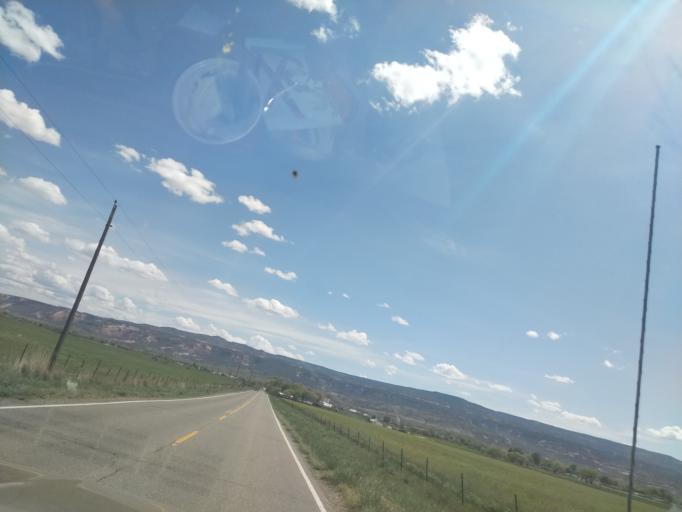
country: US
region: Colorado
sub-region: Mesa County
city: Fruita
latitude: 39.1819
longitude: -108.7571
